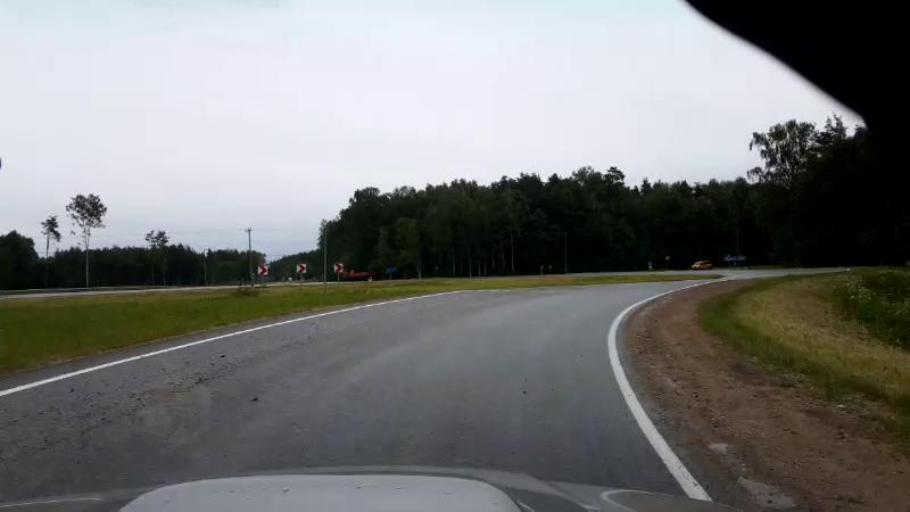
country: LV
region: Kekava
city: Kekava
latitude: 56.8134
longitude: 24.2731
